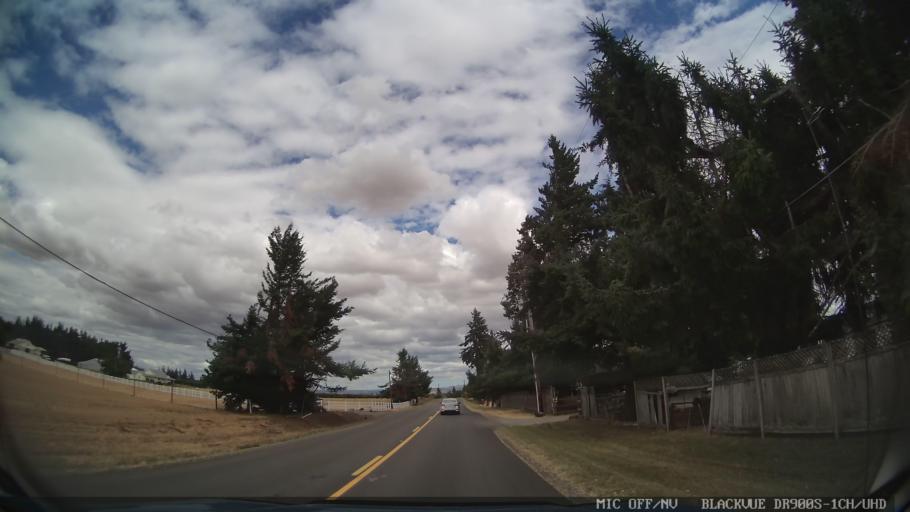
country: US
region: Oregon
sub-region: Marion County
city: Aumsville
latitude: 44.8604
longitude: -122.8568
